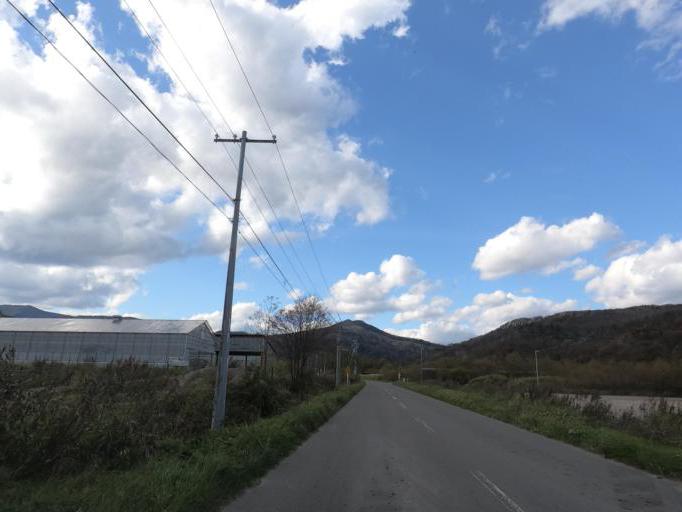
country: JP
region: Hokkaido
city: Otofuke
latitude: 43.2878
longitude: 143.2315
